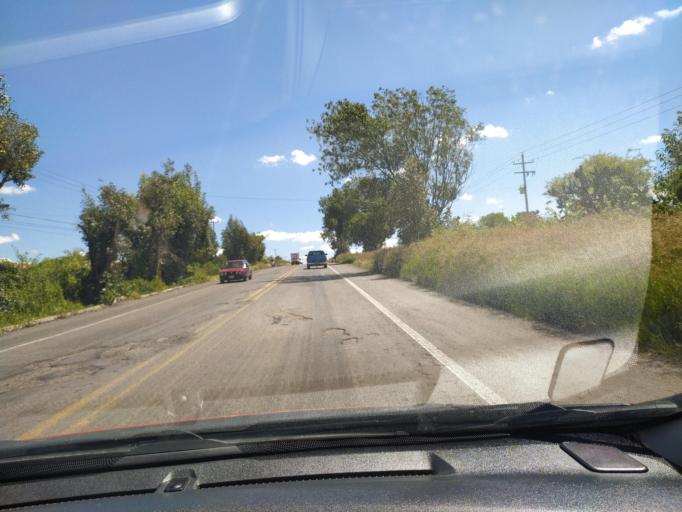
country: MX
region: Jalisco
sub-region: San Julian
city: Colonia Veintitres de Mayo
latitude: 21.0090
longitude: -102.2534
